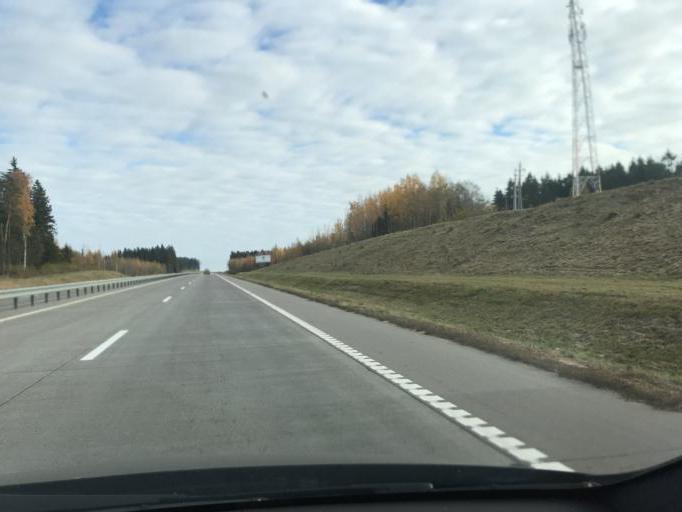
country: BY
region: Minsk
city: Pyatryshki
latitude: 54.0651
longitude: 27.2445
